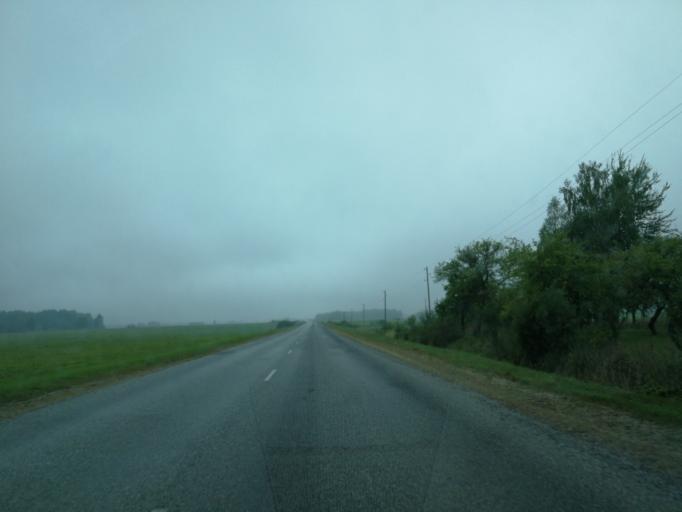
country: LV
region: Preilu Rajons
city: Preili
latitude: 56.3050
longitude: 26.6163
